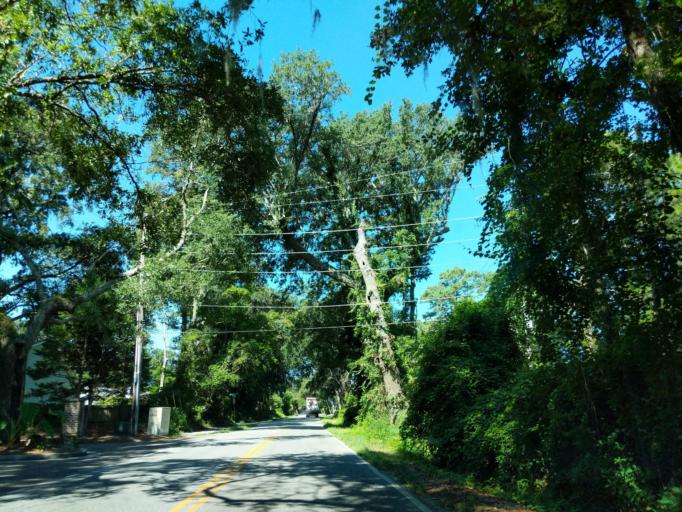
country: US
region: South Carolina
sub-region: Charleston County
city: Charleston
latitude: 32.7306
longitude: -79.9290
